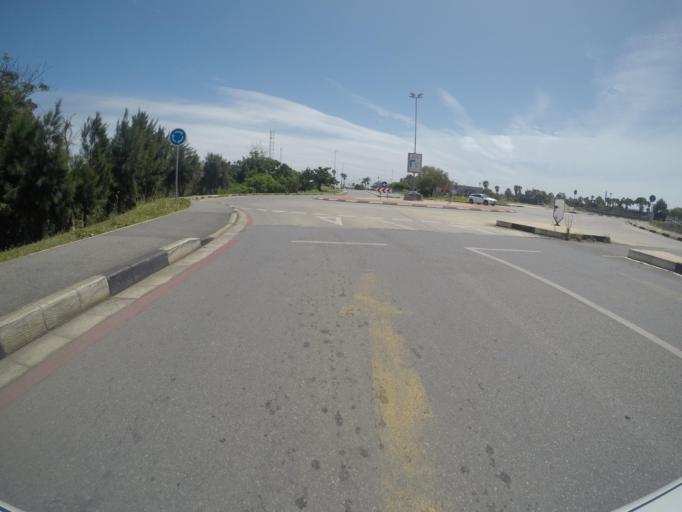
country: ZA
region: Eastern Cape
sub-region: Buffalo City Metropolitan Municipality
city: East London
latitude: -32.9365
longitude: 27.9932
